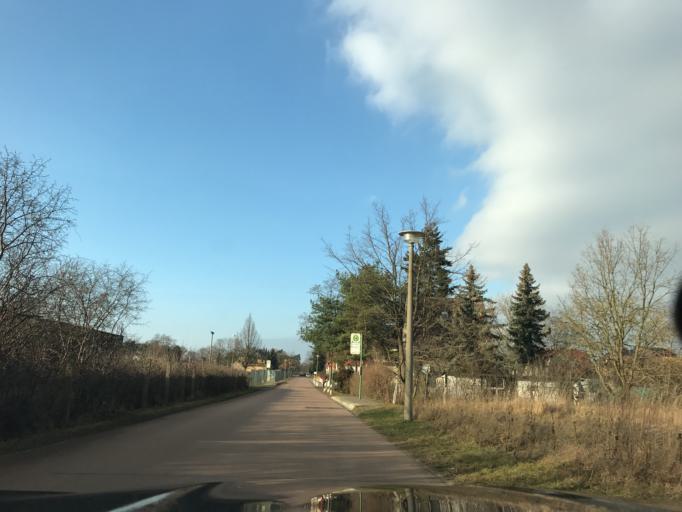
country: DE
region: Brandenburg
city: Brandenburg an der Havel
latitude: 52.3769
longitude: 12.5251
